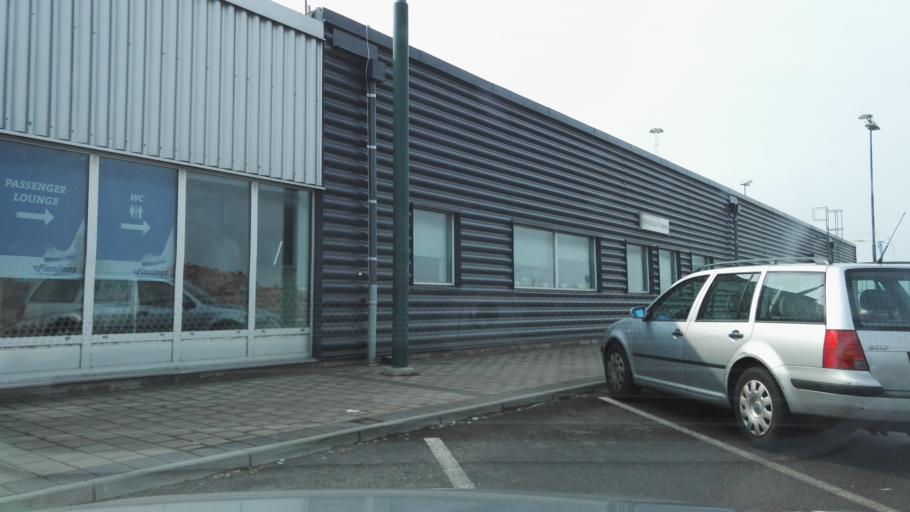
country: SE
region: Skane
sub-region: Malmo
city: Malmoe
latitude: 55.6295
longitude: 13.0093
